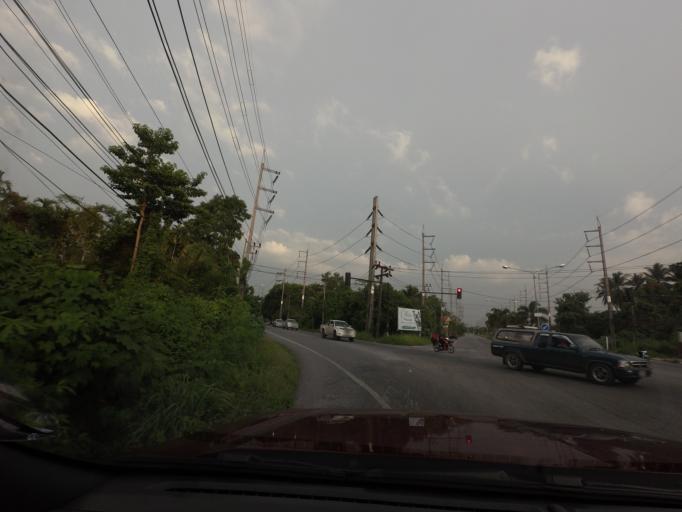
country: TH
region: Yala
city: Yala
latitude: 6.5749
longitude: 101.1995
